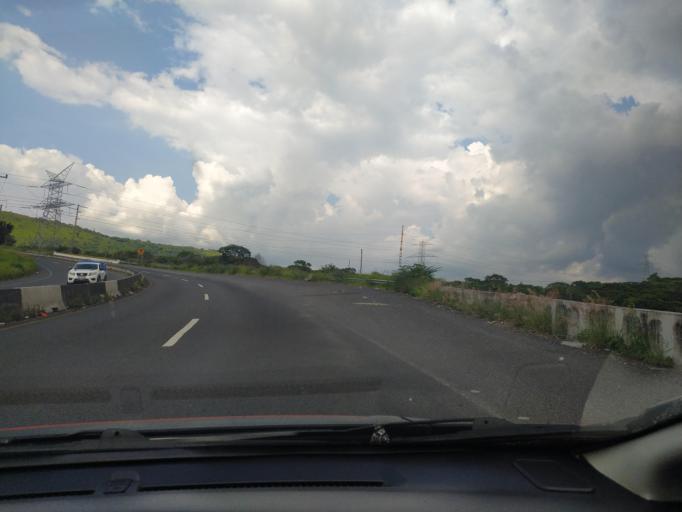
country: MX
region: Jalisco
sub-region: Acatlan de Juarez
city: Villa de los Ninos
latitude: 20.4289
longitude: -103.5823
